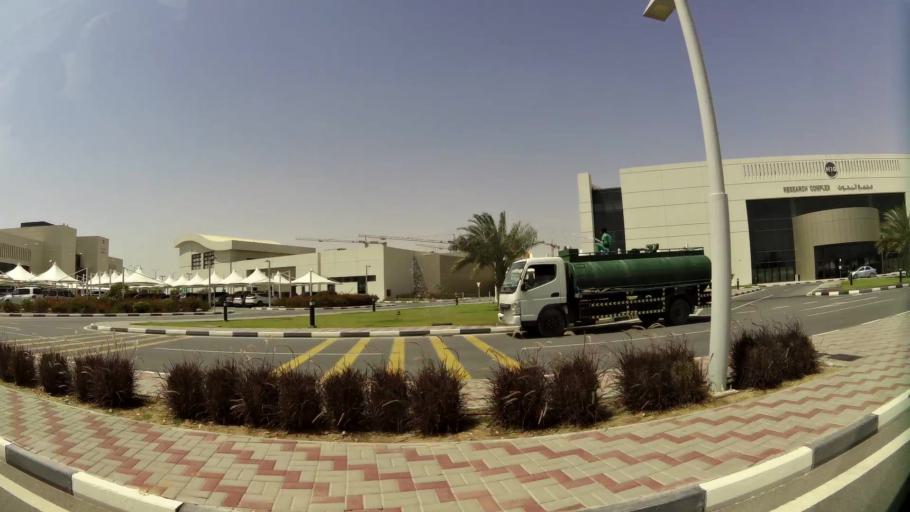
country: QA
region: Baladiyat Umm Salal
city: Umm Salal Muhammad
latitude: 25.3794
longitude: 51.4905
